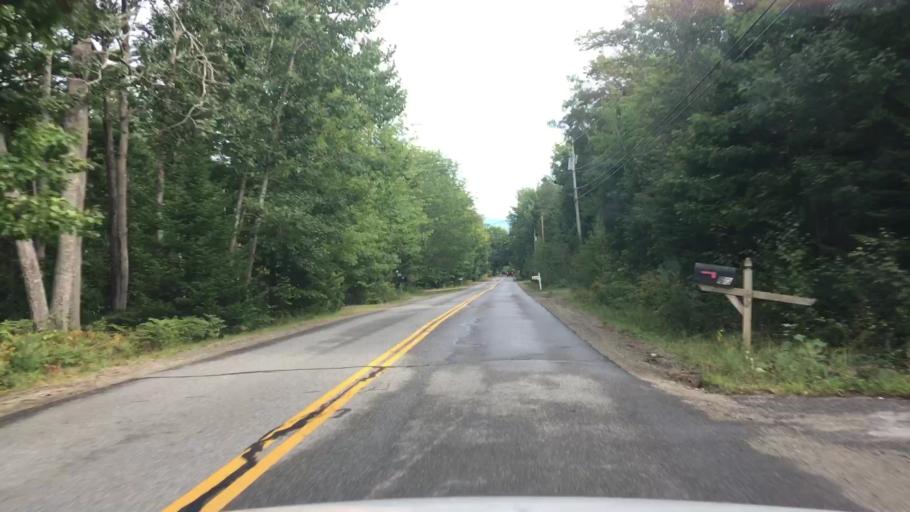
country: US
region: Maine
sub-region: Hancock County
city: Trenton
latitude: 44.4382
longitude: -68.4016
